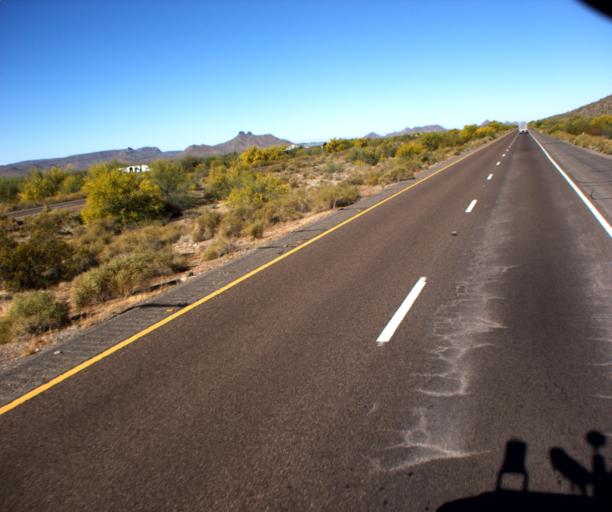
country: US
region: Arizona
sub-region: Maricopa County
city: Gila Bend
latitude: 32.8593
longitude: -112.3902
